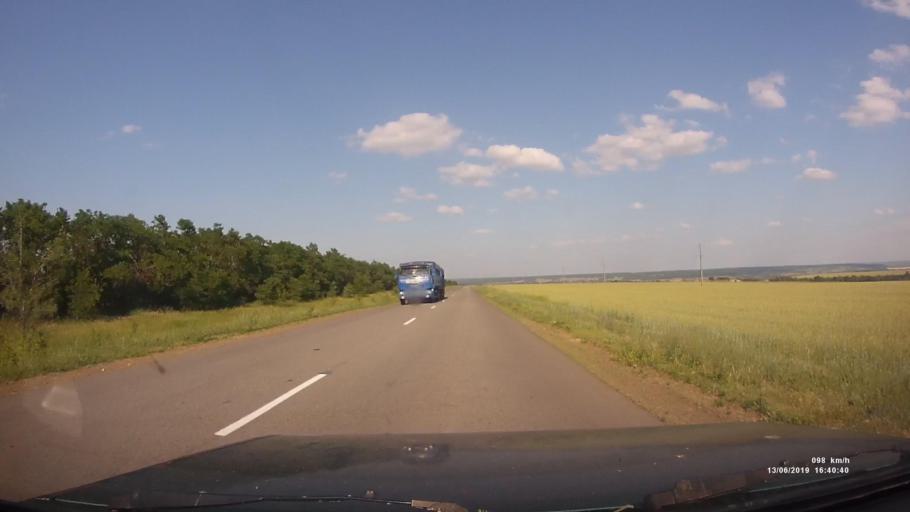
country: RU
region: Rostov
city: Kazanskaya
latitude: 49.9329
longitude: 41.3665
